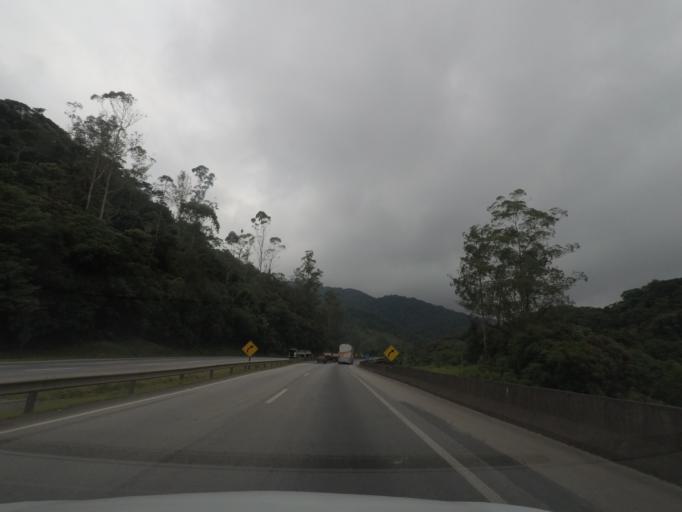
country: BR
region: Sao Paulo
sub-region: Juquitiba
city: Juquitiba
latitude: -24.0408
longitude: -47.1932
